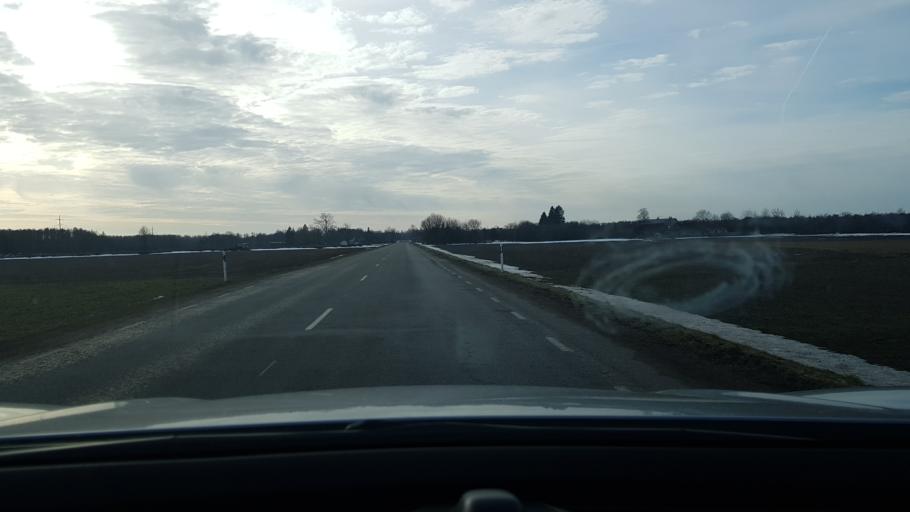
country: EE
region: Saare
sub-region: Kuressaare linn
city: Kuressaare
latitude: 58.3145
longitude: 22.5445
